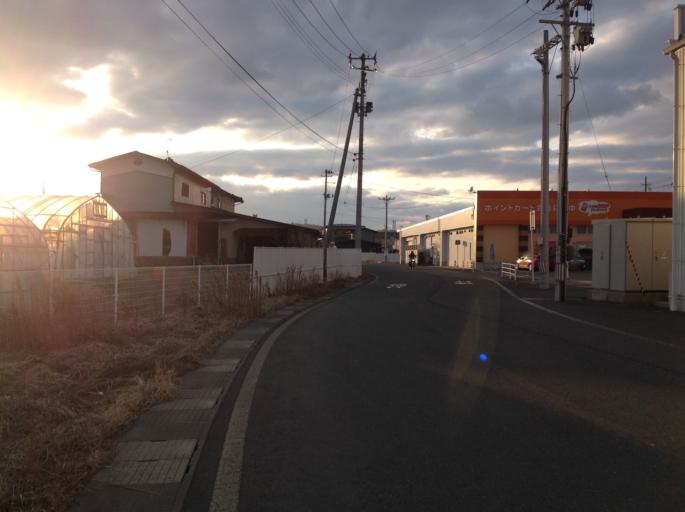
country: JP
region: Iwate
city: Ichinoseki
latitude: 38.9386
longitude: 141.1495
